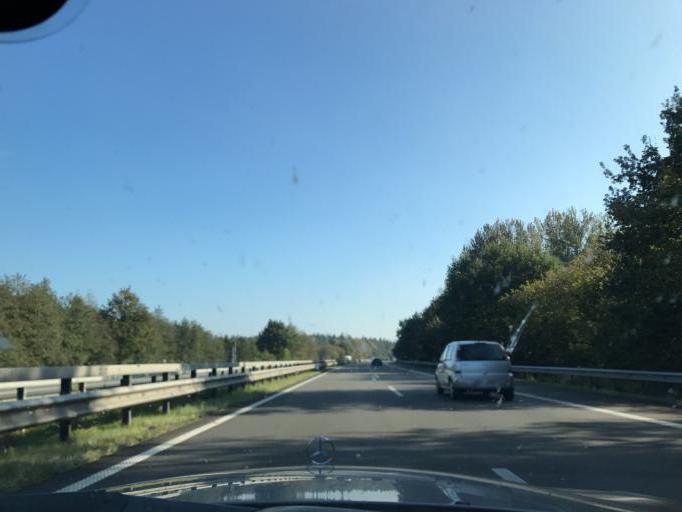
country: DE
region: Lower Saxony
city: Bad Zwischenahn
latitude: 53.2449
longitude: 8.0155
